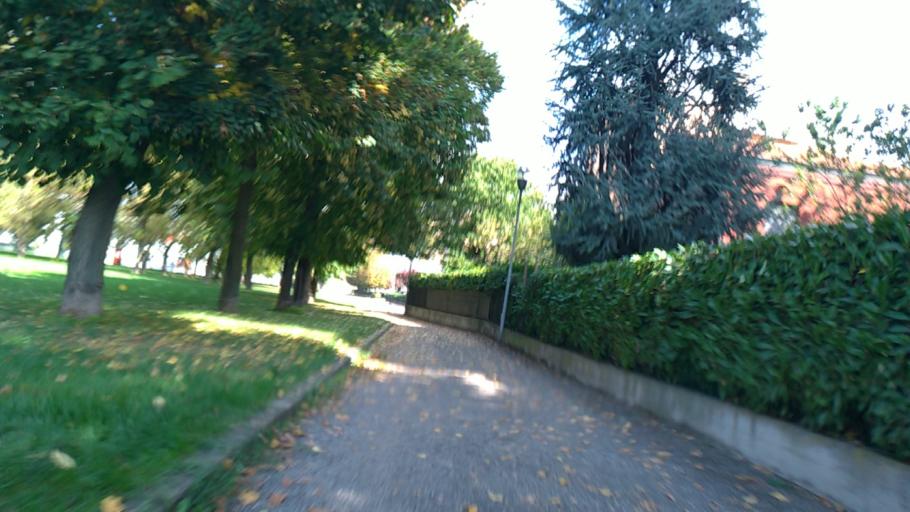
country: IT
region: Emilia-Romagna
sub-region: Provincia di Modena
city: Carpi Centro
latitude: 44.7701
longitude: 10.8721
